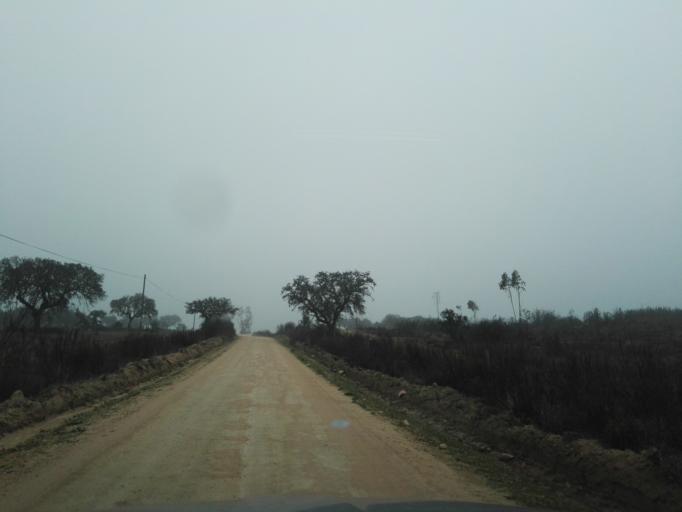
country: PT
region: Evora
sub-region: Montemor-O-Novo
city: Montemor-o-Novo
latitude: 38.7843
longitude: -8.2262
